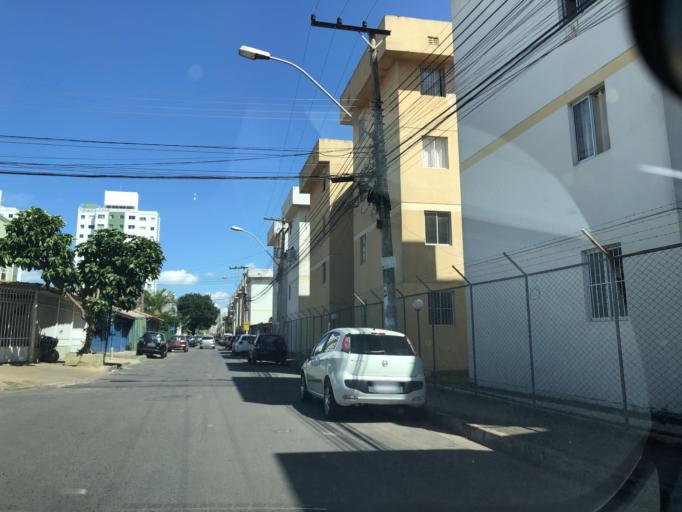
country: BR
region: Federal District
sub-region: Brasilia
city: Brasilia
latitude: -15.8676
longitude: -48.0641
